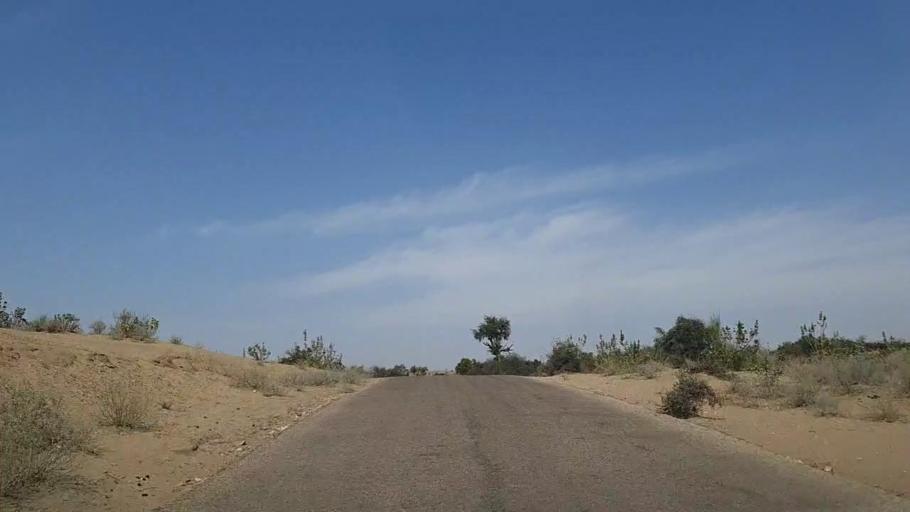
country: PK
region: Sindh
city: Nabisar
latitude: 25.0990
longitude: 69.9929
